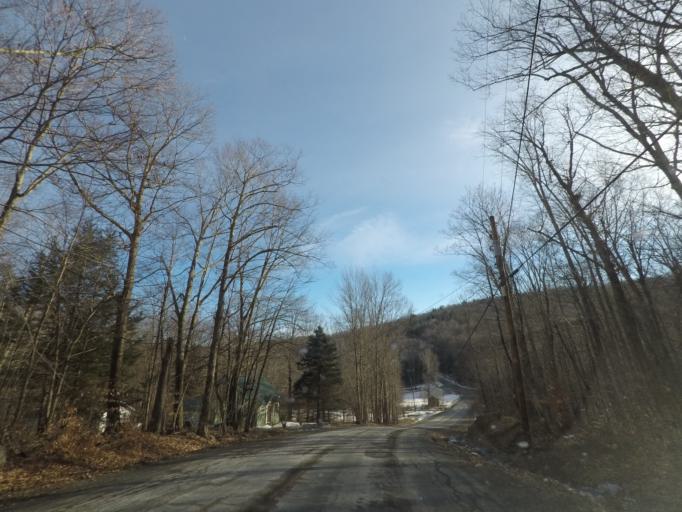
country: US
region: New York
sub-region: Rensselaer County
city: Hoosick Falls
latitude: 42.7380
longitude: -73.3807
